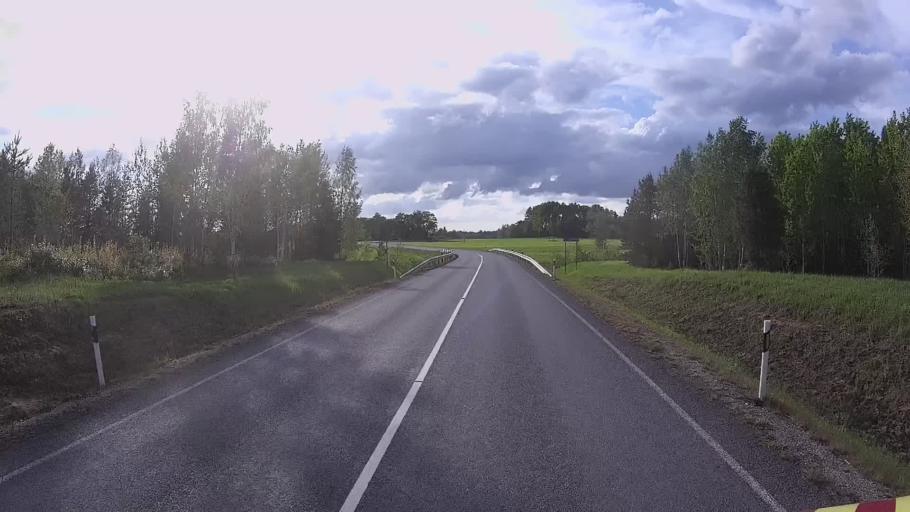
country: EE
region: Jogevamaa
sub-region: Mustvee linn
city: Mustvee
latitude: 59.0484
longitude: 27.0307
